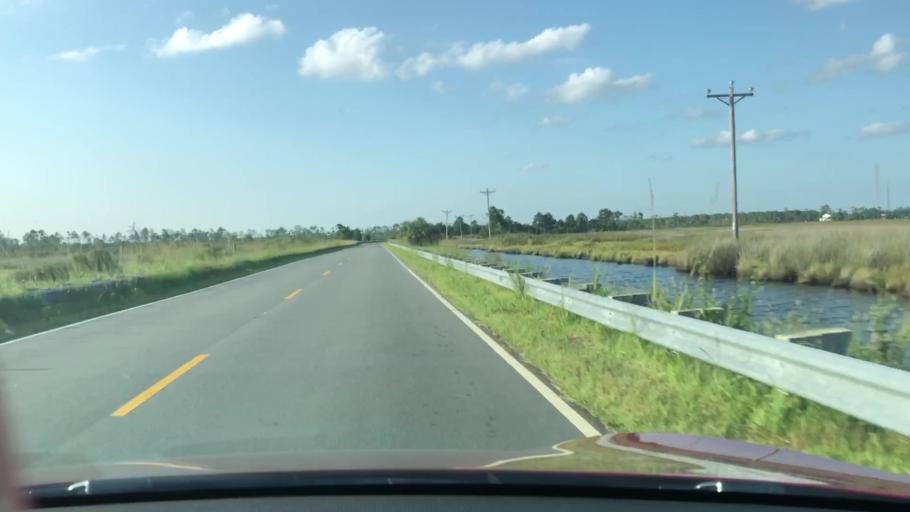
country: US
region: North Carolina
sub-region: Dare County
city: Wanchese
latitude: 35.6868
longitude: -75.7806
